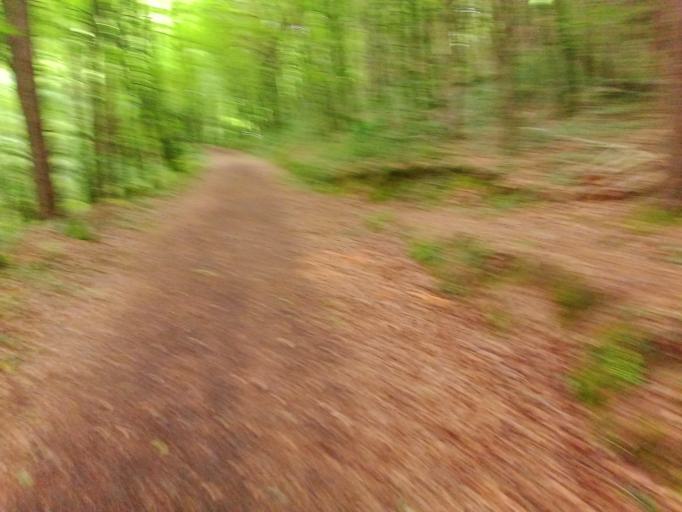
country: IE
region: Leinster
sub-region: Laois
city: Stradbally
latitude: 52.9985
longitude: -7.1167
